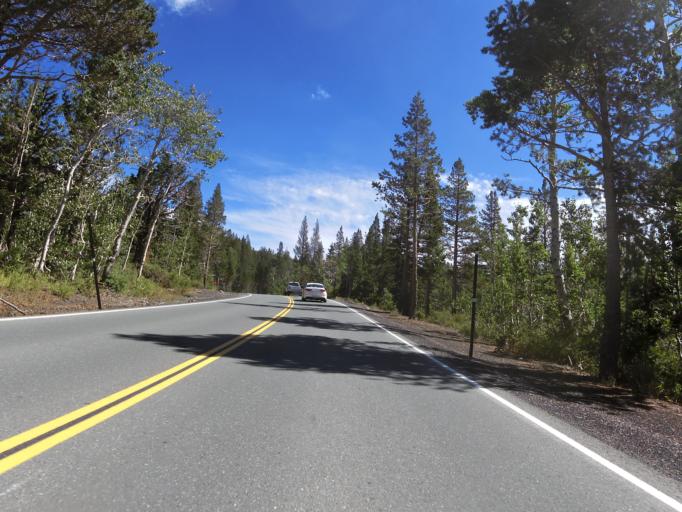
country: US
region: California
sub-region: El Dorado County
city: South Lake Tahoe
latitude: 38.7001
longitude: -120.0238
